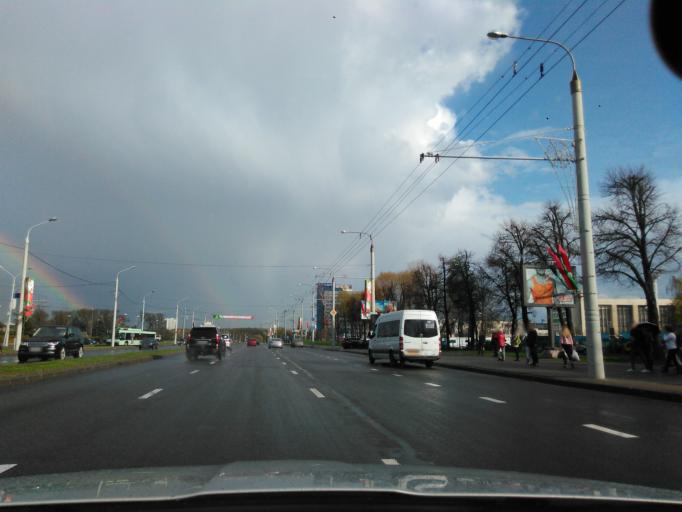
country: BY
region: Minsk
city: Minsk
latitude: 53.9268
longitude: 27.5191
